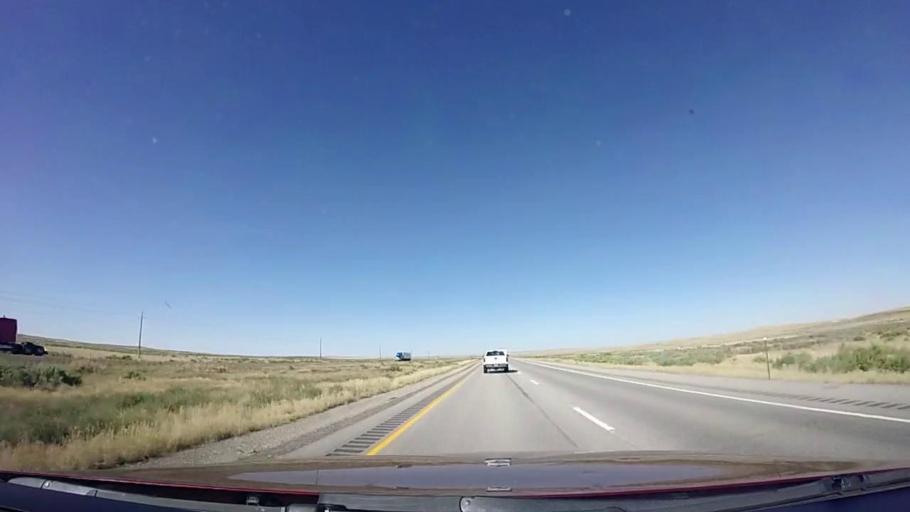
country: US
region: Wyoming
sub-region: Carbon County
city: Rawlins
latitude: 41.7834
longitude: -107.4208
